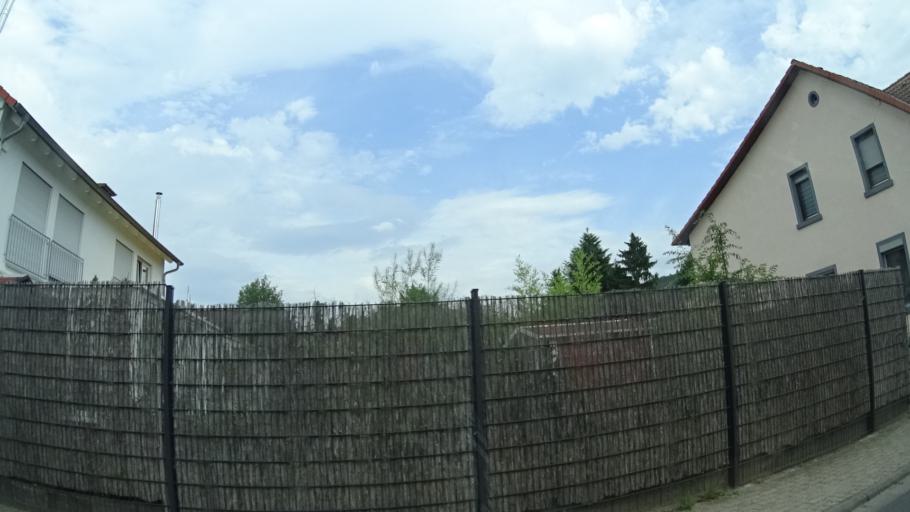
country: DE
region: Hesse
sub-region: Regierungsbezirk Darmstadt
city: Bickenbach
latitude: 49.7545
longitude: 8.6341
